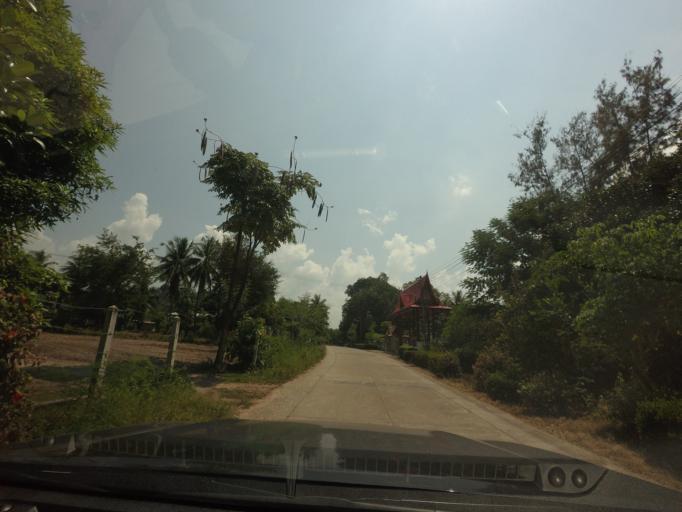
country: TH
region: Uttaradit
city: Thong Saen Khan
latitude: 17.4562
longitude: 100.3093
